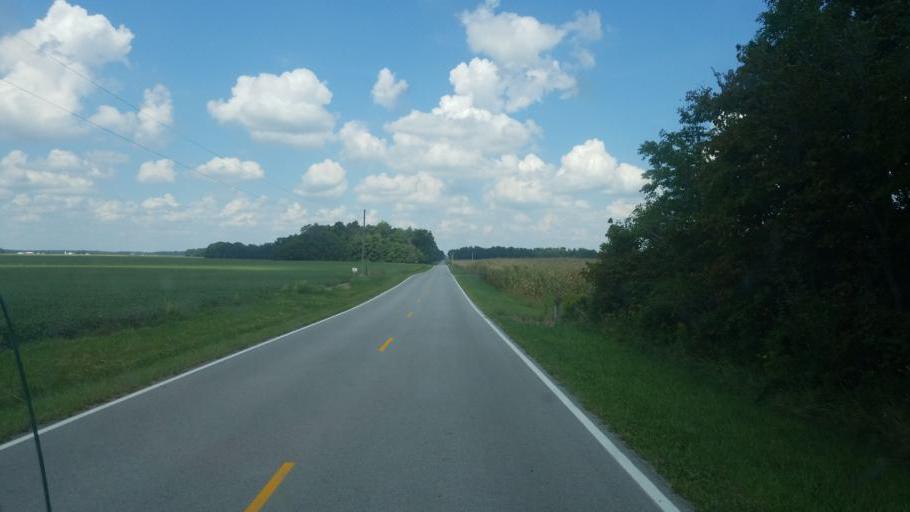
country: US
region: Ohio
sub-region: Hancock County
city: Arlington
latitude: 40.8373
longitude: -83.7277
